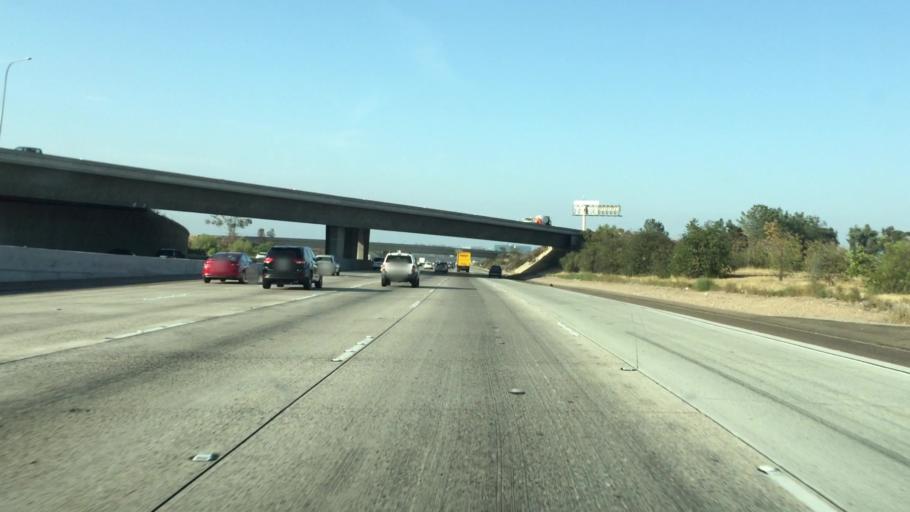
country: US
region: California
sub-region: San Diego County
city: La Mesa
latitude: 32.8583
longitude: -117.1138
